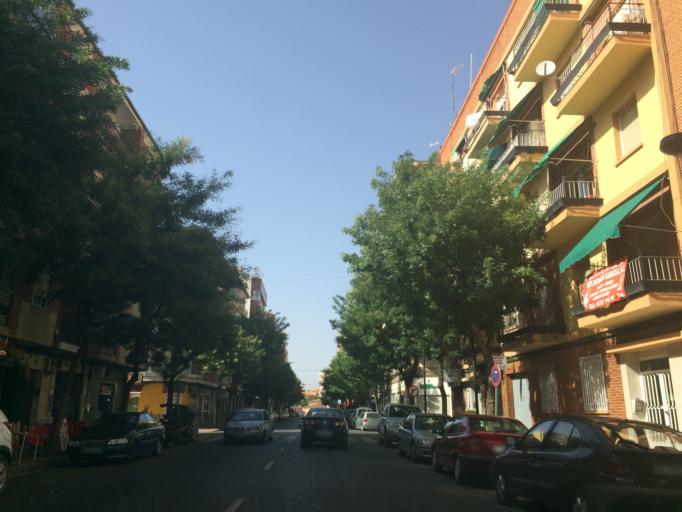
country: ES
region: Castille-La Mancha
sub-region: Provincia de Albacete
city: Albacete
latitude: 38.9943
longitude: -1.8671
